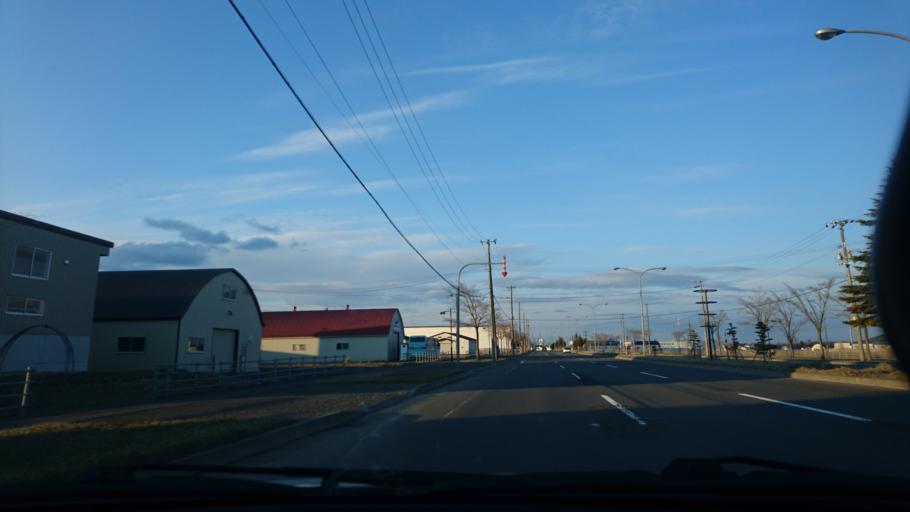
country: JP
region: Hokkaido
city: Sapporo
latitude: 43.1097
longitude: 141.3980
